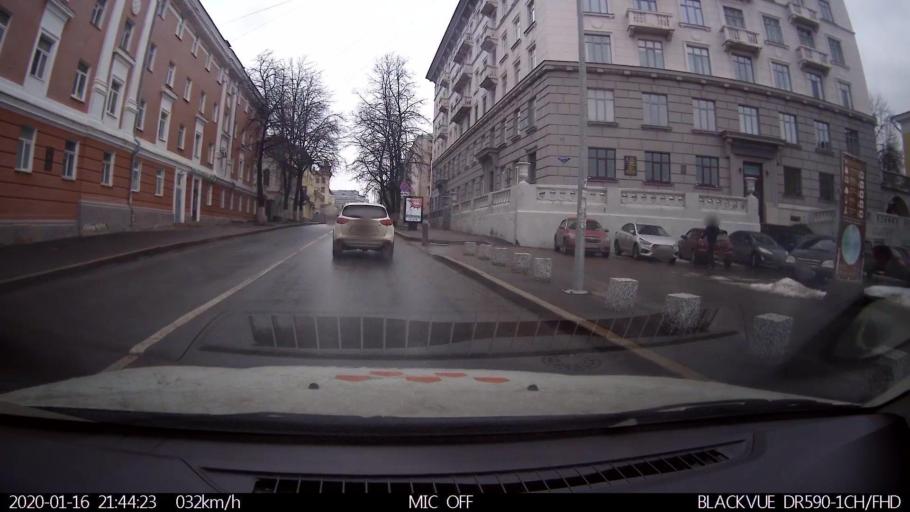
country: RU
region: Nizjnij Novgorod
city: Nizhniy Novgorod
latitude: 56.3303
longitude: 44.0070
